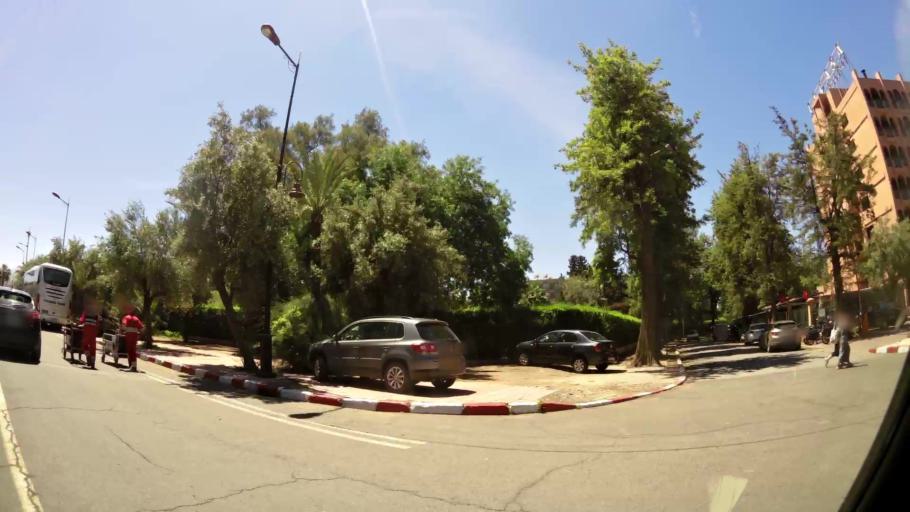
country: MA
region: Marrakech-Tensift-Al Haouz
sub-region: Marrakech
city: Marrakesh
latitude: 31.6205
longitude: -8.0064
